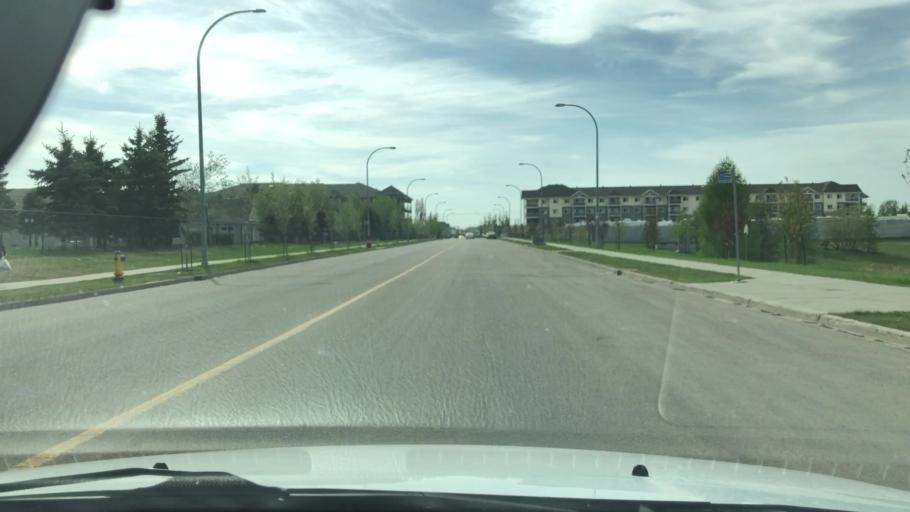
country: CA
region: Alberta
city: Edmonton
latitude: 53.6042
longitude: -113.5352
